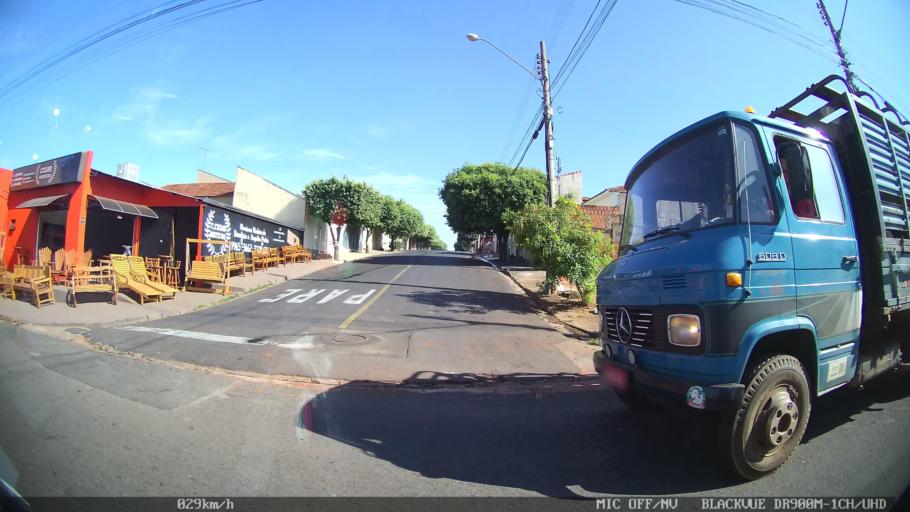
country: BR
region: Sao Paulo
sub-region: Sao Jose Do Rio Preto
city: Sao Jose do Rio Preto
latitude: -20.7852
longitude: -49.3879
